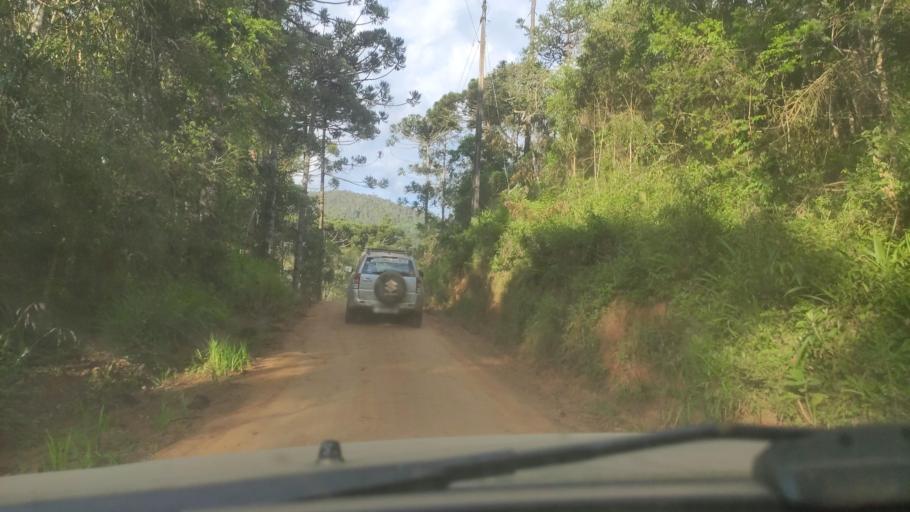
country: BR
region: Minas Gerais
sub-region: Cambui
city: Cambui
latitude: -22.7591
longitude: -45.9547
